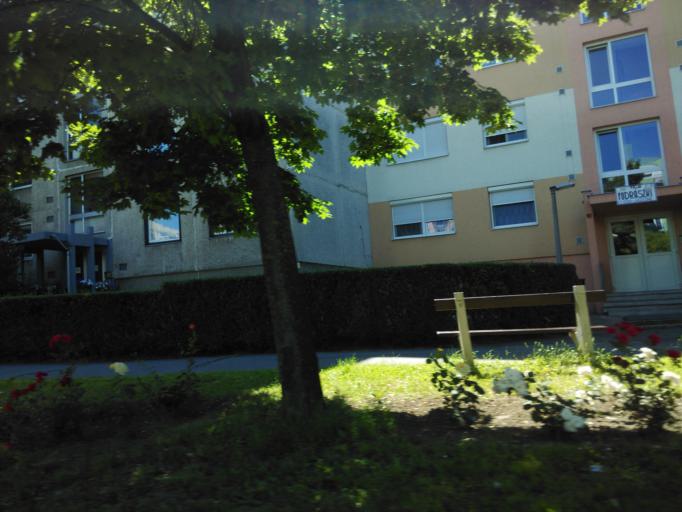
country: HU
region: Fejer
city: Mor
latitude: 47.3705
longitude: 18.2102
